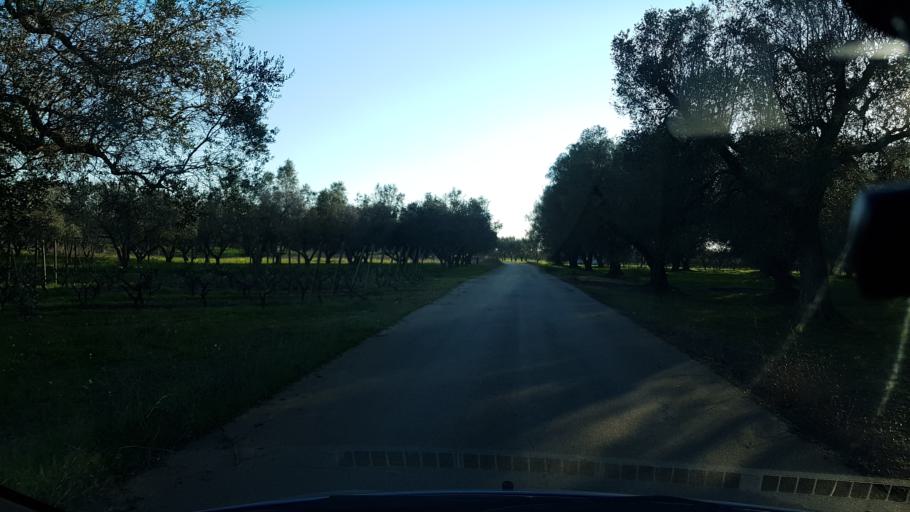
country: IT
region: Apulia
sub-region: Provincia di Brindisi
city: Mesagne
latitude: 40.5602
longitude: 17.8656
